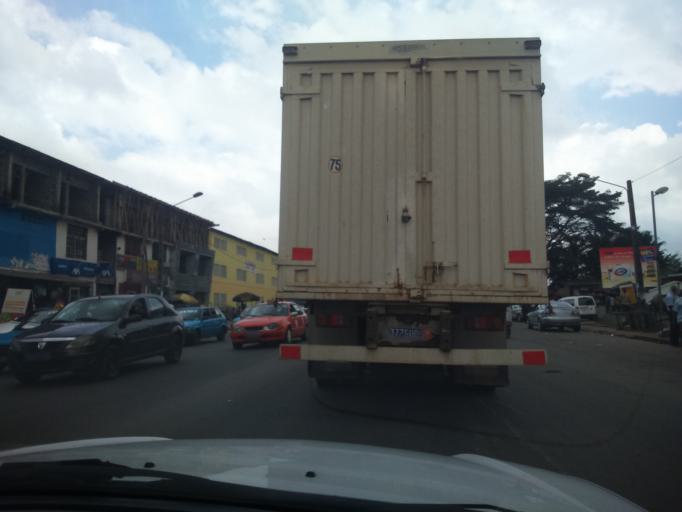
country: CI
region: Lagunes
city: Abidjan
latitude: 5.3469
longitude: -4.0634
